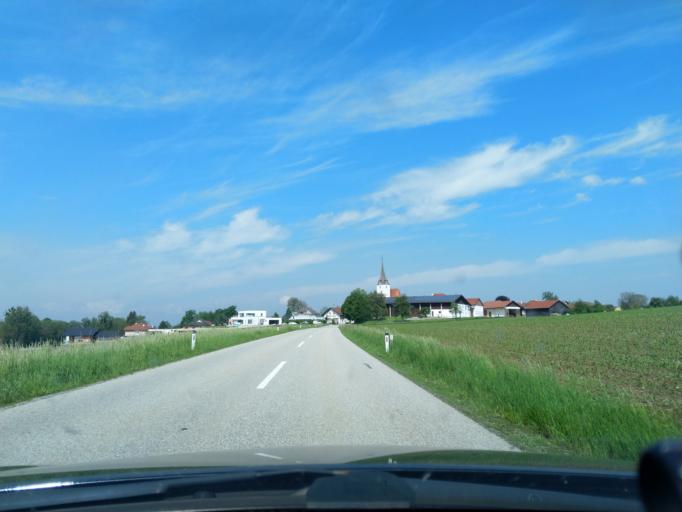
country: DE
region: Bavaria
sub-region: Lower Bavaria
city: Bad Fussing
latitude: 48.3014
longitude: 13.3689
